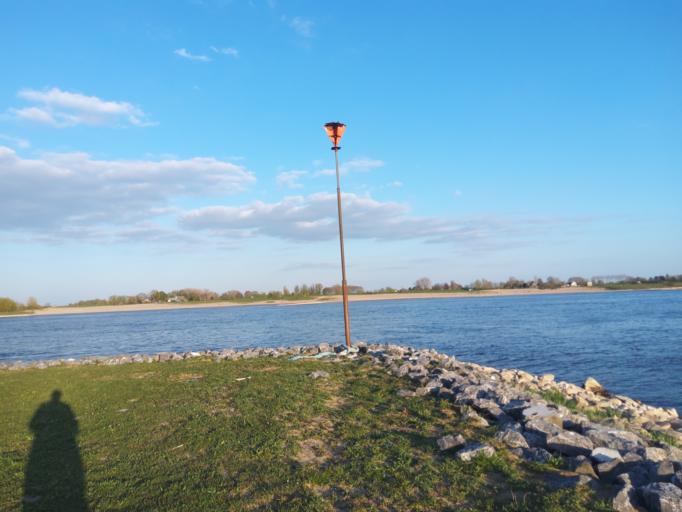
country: NL
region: Gelderland
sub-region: Gemeente Maasdriel
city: Heerewaarden
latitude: 51.8269
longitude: 5.3827
